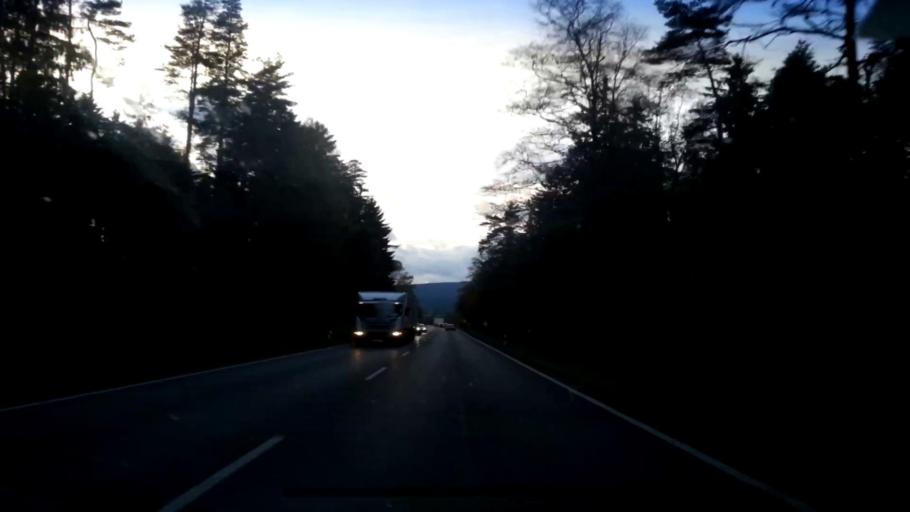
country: DE
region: Bavaria
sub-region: Upper Franconia
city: Trostau
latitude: 50.0175
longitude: 11.9764
